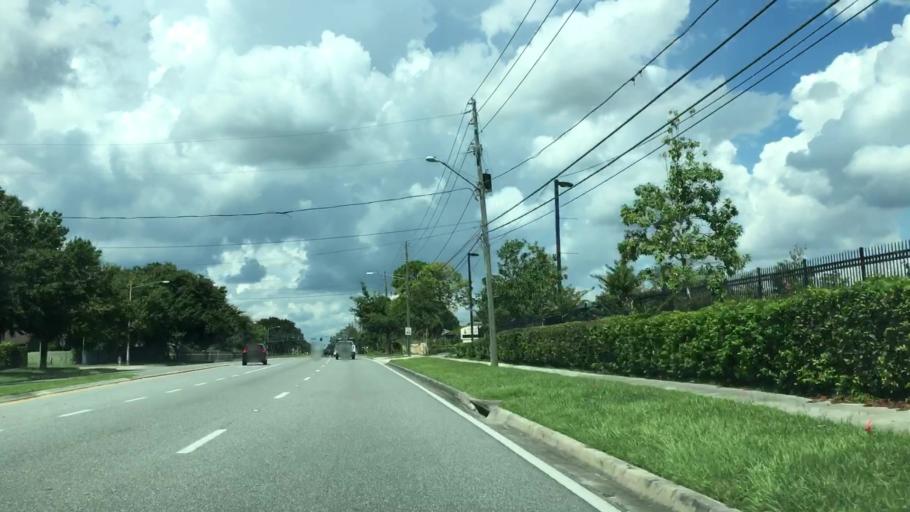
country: US
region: Florida
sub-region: Orange County
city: Conway
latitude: 28.4991
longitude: -81.2903
